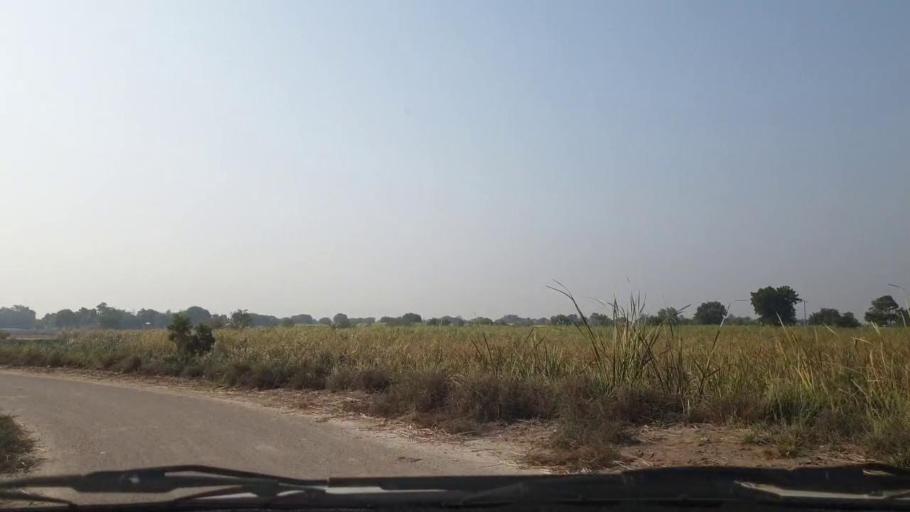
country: PK
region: Sindh
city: Tando Muhammad Khan
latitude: 25.0086
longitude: 68.4507
